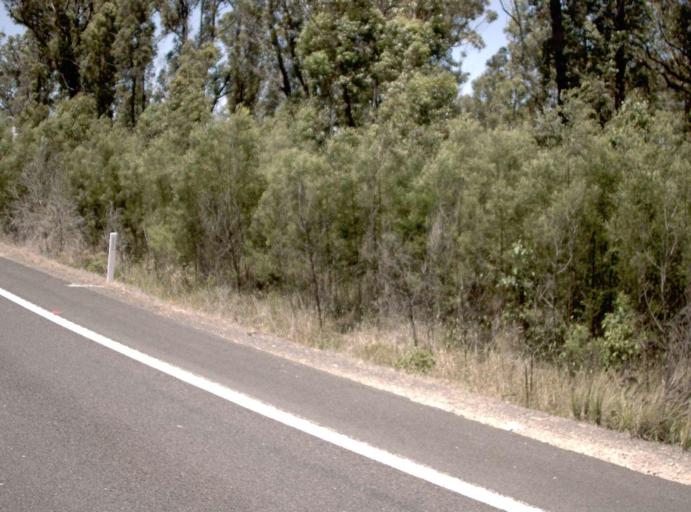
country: AU
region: Victoria
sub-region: East Gippsland
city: Lakes Entrance
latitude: -37.7532
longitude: 148.2833
